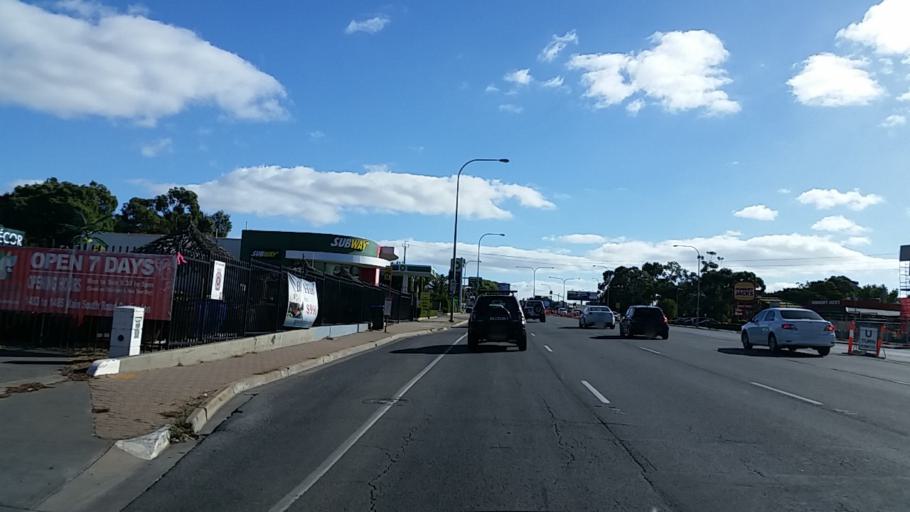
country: AU
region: South Australia
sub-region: Marion
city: Marion
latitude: -35.0245
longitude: 138.5615
